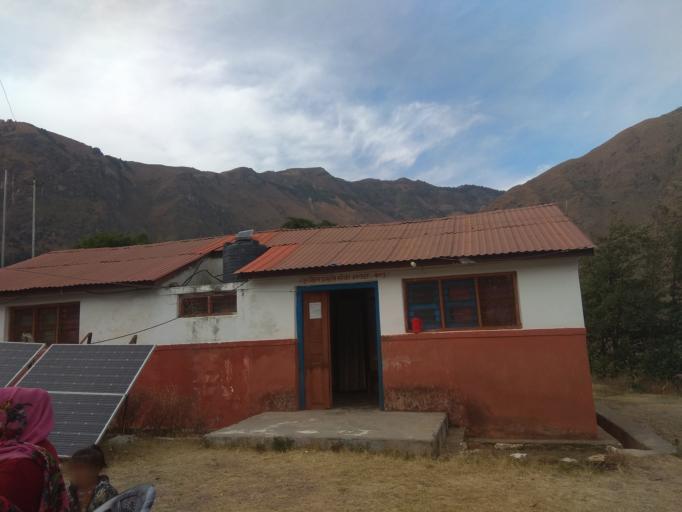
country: NP
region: Mid Western
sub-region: Bheri Zone
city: Dailekh
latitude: 29.2515
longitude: 81.6683
